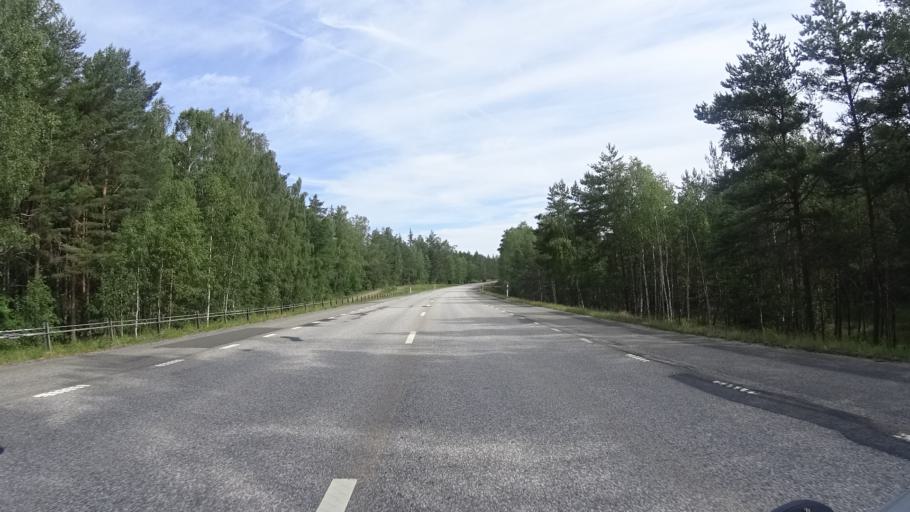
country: SE
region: Kalmar
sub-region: Vasterviks Kommun
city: Ankarsrum
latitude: 57.6909
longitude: 16.4398
